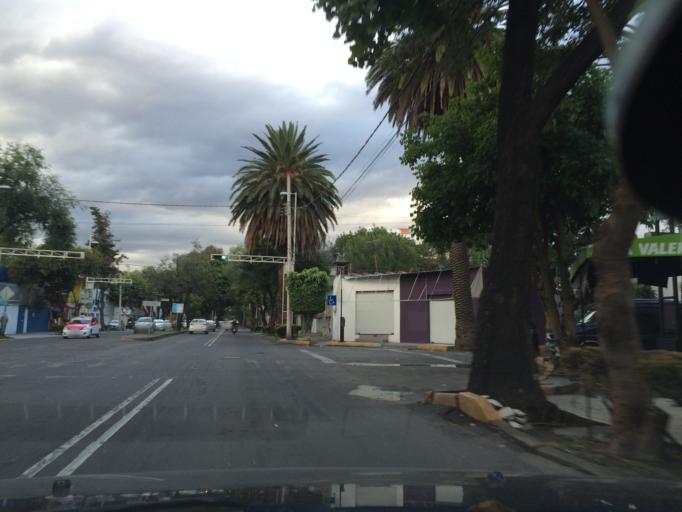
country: MX
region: Mexico City
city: Colonia Nativitas
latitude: 19.3653
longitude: -99.1488
